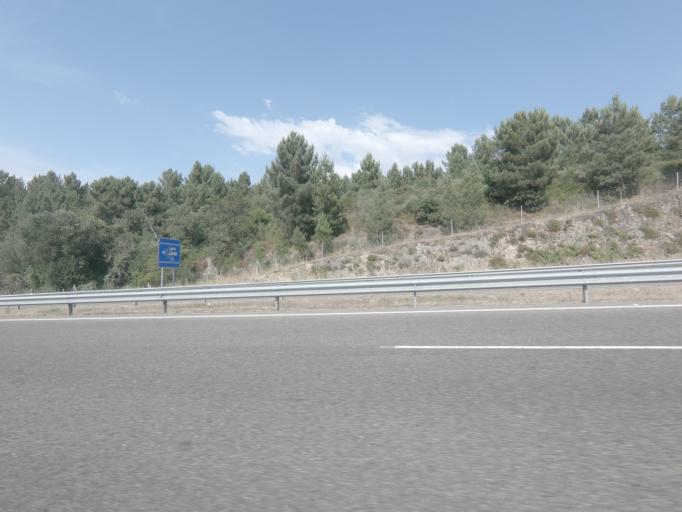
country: ES
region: Galicia
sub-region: Provincia de Ourense
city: Taboadela
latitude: 42.2739
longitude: -7.8723
